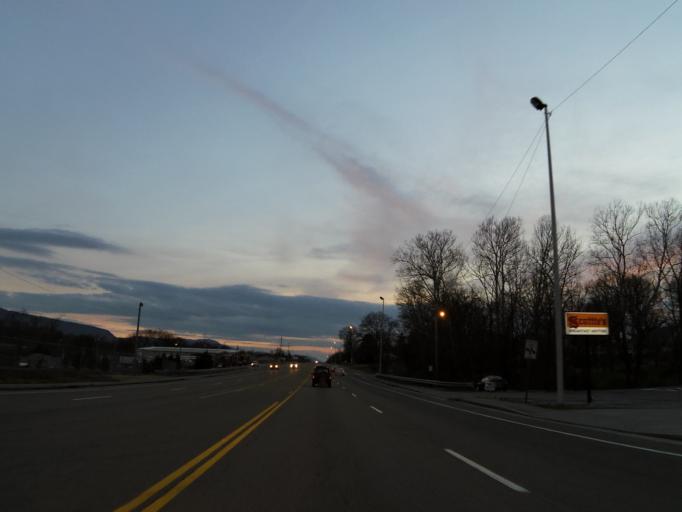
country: US
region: Tennessee
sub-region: McMinn County
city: Etowah
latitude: 35.3186
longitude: -84.5280
